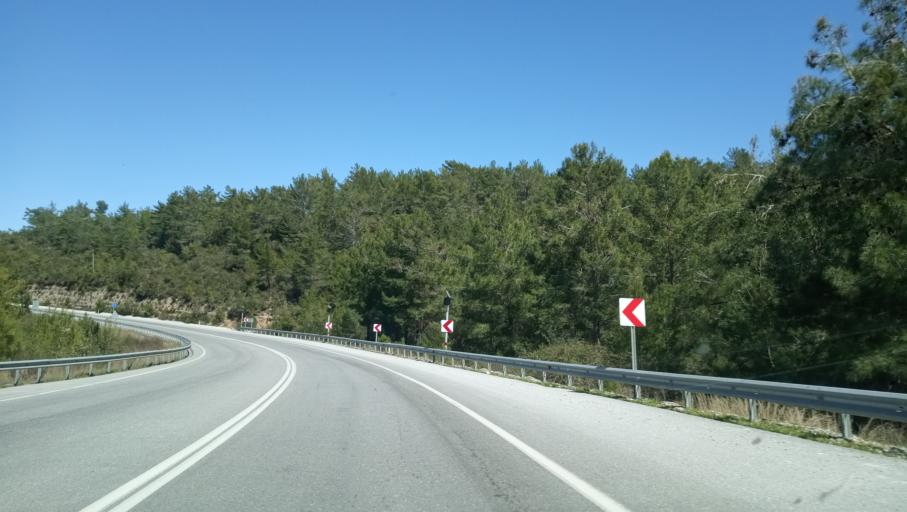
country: TR
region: Antalya
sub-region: Alanya
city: Okurcalar
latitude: 36.7679
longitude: 31.6741
